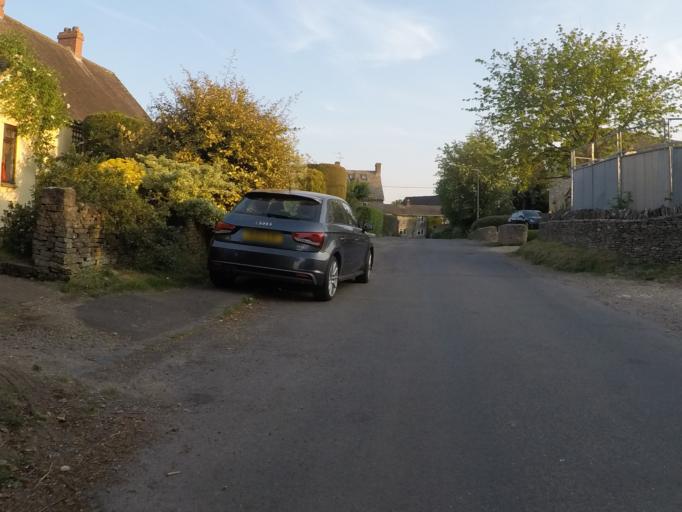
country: GB
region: England
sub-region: Oxfordshire
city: Charlbury
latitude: 51.8377
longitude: -1.5336
